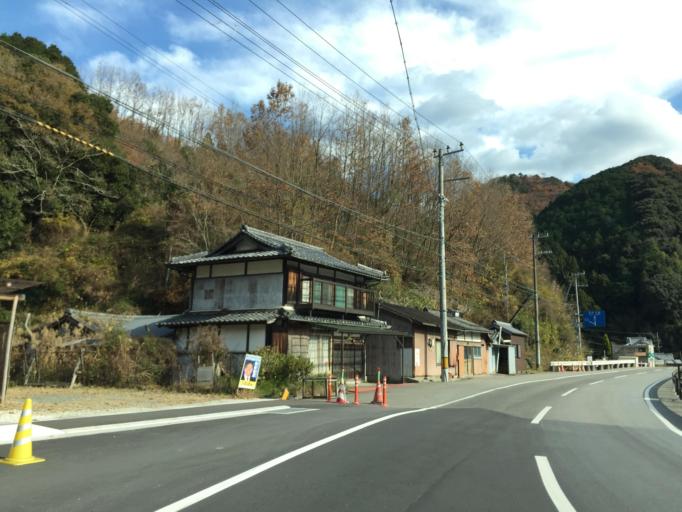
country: JP
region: Wakayama
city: Iwade
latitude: 34.1434
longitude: 135.3833
